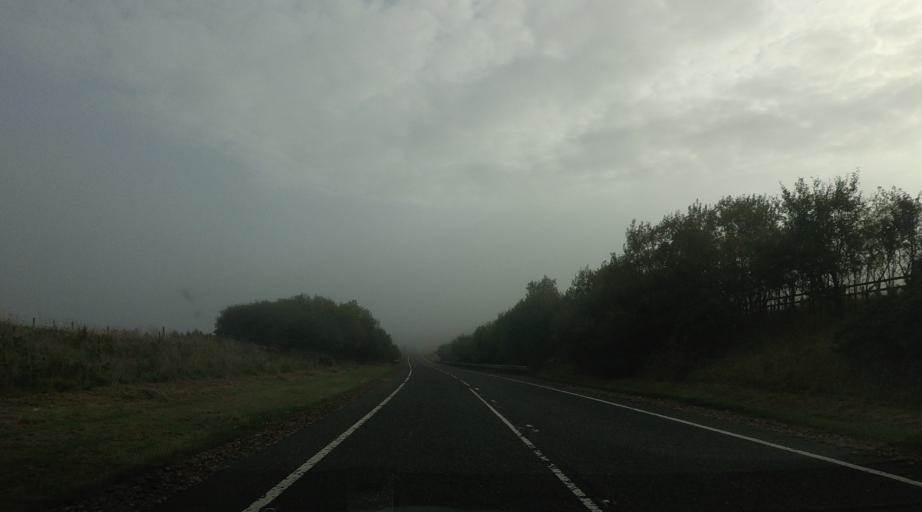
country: GB
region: Scotland
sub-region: Highland
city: Brora
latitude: 58.1277
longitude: -3.6330
